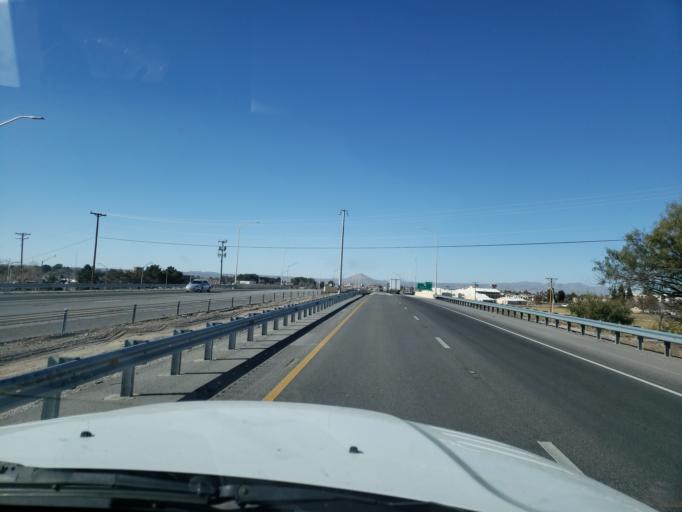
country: US
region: New Mexico
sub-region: Dona Ana County
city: University Park
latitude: 32.2768
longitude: -106.7607
